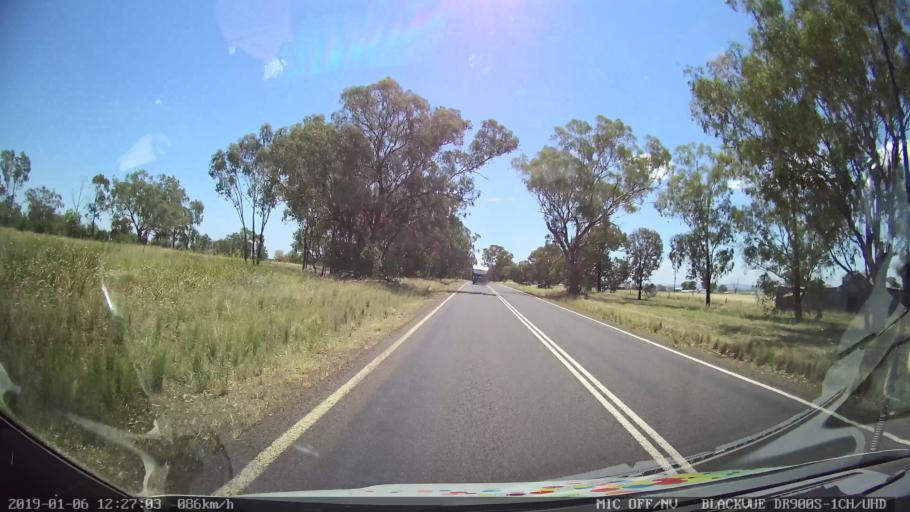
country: AU
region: New South Wales
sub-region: Tamworth Municipality
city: Phillip
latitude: -31.2111
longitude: 150.8248
